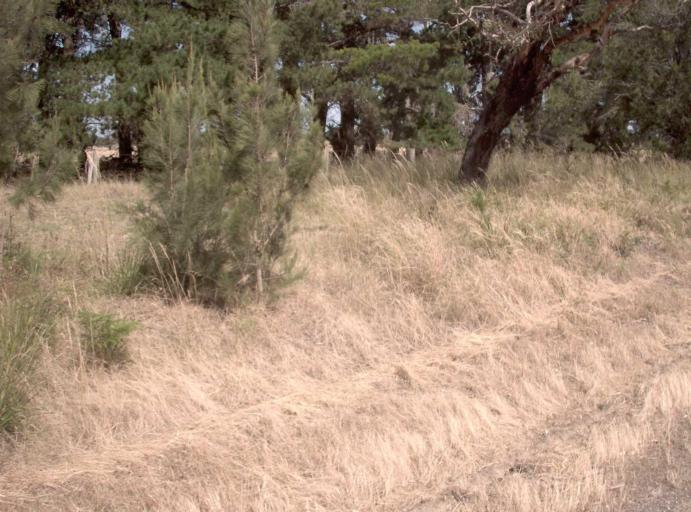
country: AU
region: Victoria
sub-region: Wellington
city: Sale
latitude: -38.3125
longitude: 147.1544
